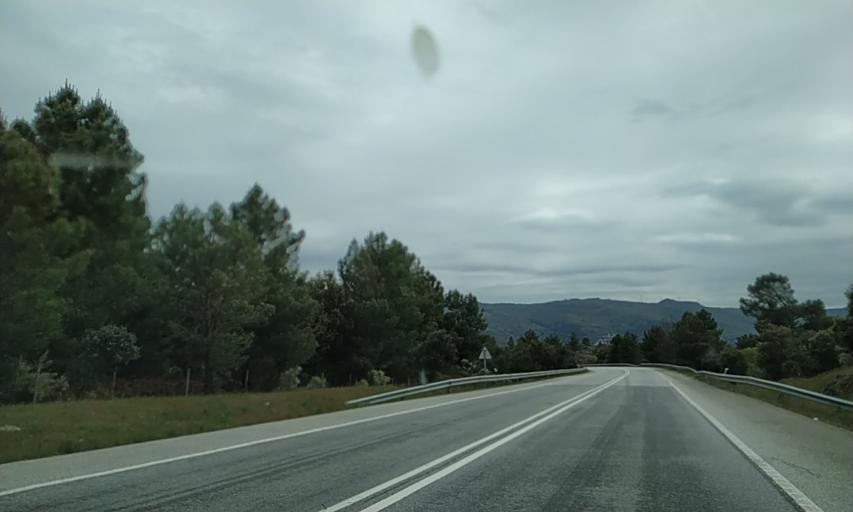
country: PT
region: Guarda
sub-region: Celorico da Beira
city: Celorico da Beira
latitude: 40.6265
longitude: -7.3073
